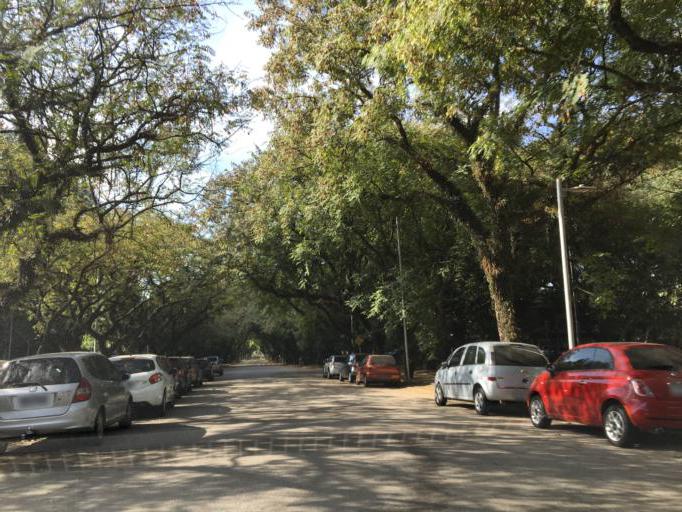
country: BR
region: Sao Paulo
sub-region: Osasco
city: Osasco
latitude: -23.5573
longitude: -46.7267
